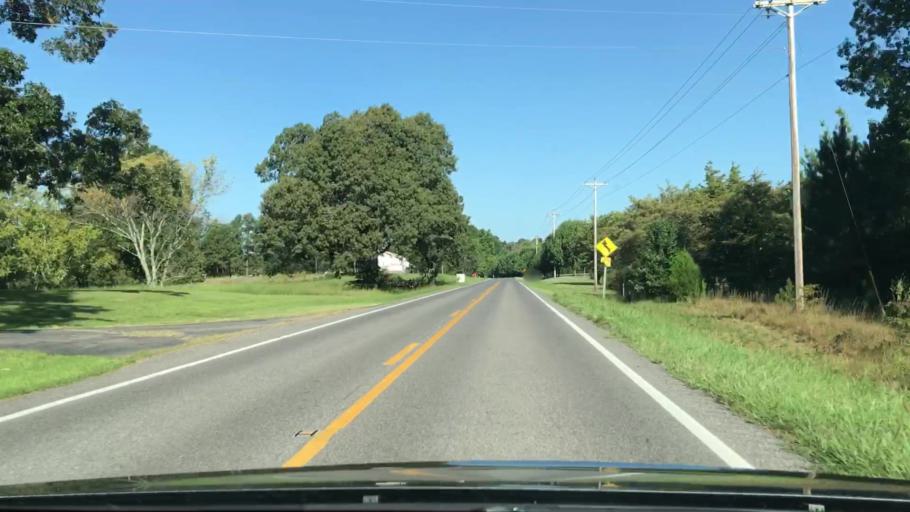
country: US
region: Kentucky
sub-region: Graves County
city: Mayfield
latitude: 36.7771
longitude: -88.5090
